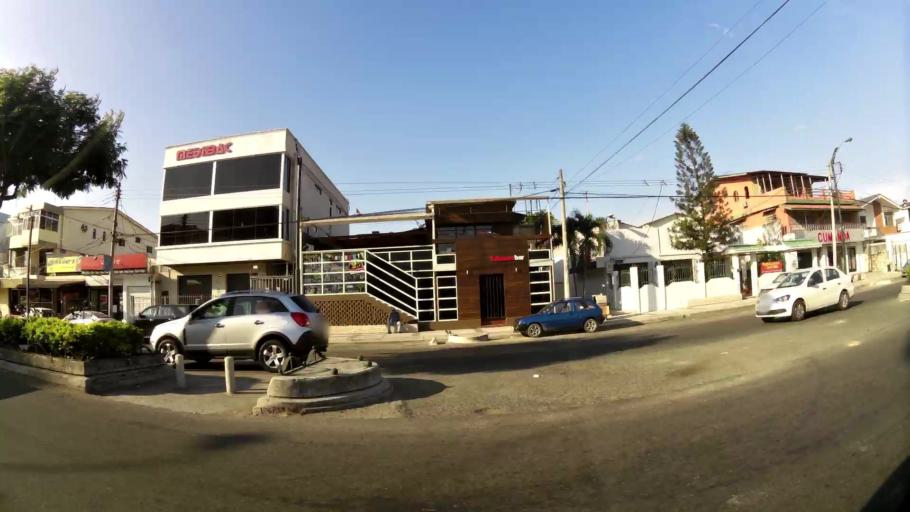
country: EC
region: Guayas
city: Guayaquil
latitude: -2.1639
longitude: -79.9129
